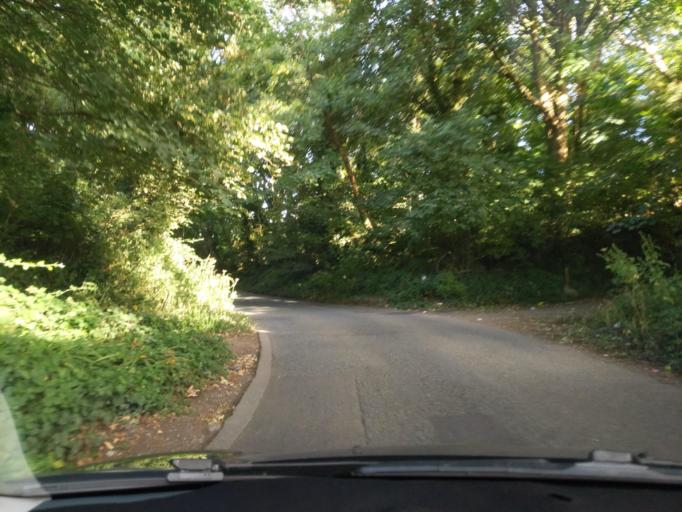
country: GB
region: England
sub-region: Plymouth
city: Plymstock
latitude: 50.3912
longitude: -4.1001
